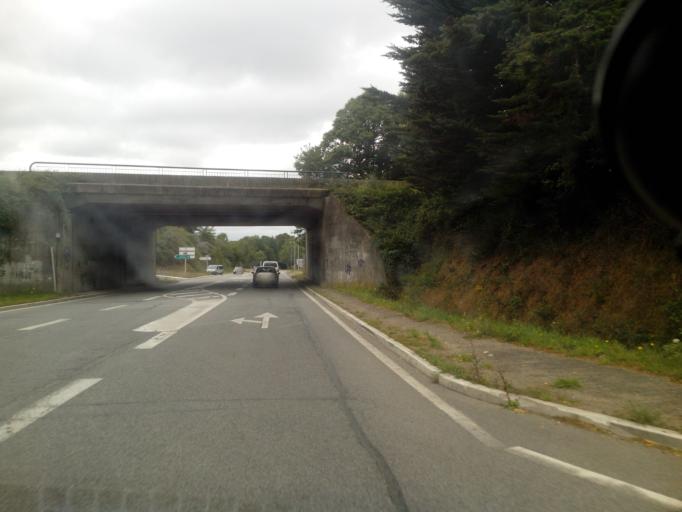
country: FR
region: Brittany
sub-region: Departement du Morbihan
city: Hennebont
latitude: 47.7878
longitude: -3.2771
